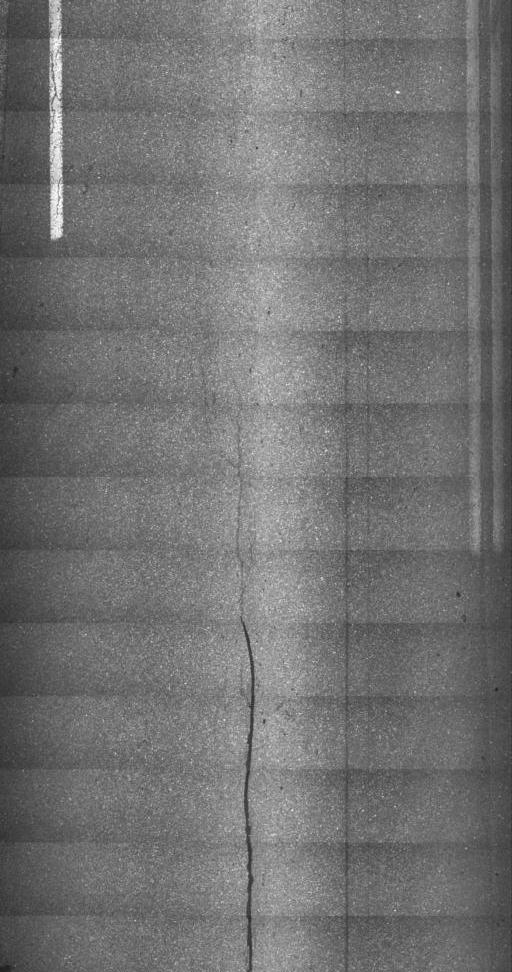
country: US
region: Vermont
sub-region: Chittenden County
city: Milton
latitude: 44.6319
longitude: -73.1152
